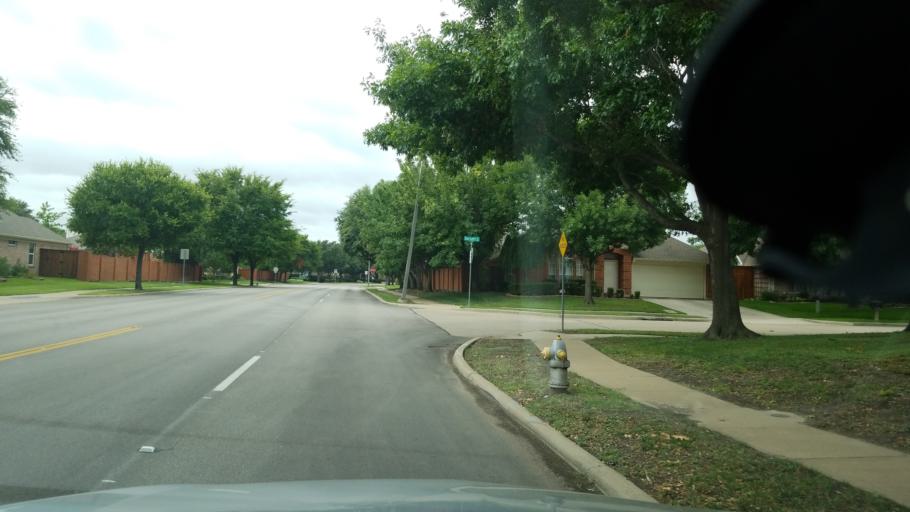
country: US
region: Texas
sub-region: Dallas County
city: Farmers Branch
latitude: 32.9426
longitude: -96.9446
